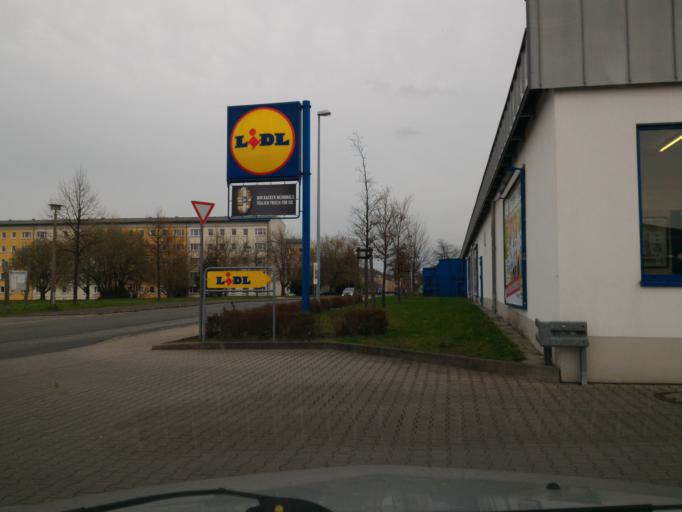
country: DE
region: Saxony
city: Zittau
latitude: 50.8867
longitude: 14.8017
